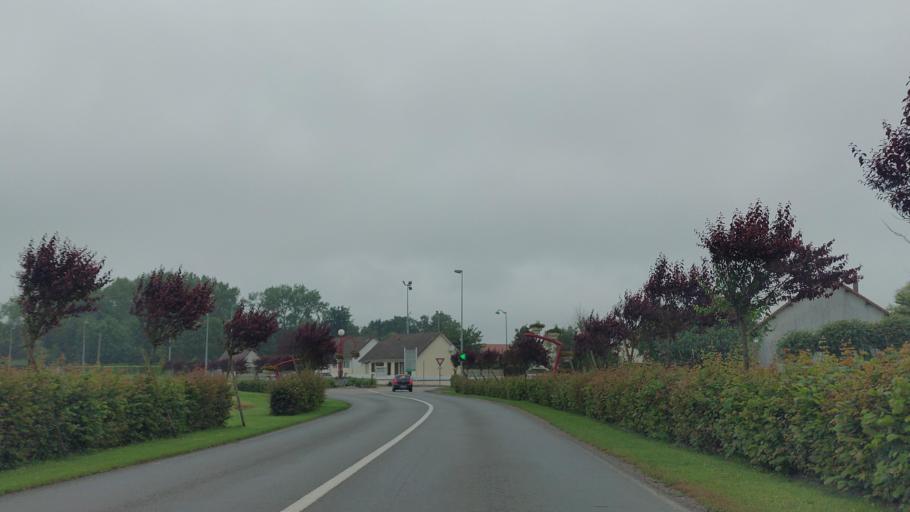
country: FR
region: Picardie
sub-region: Departement de la Somme
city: Bethencourt-sur-Mer
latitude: 50.0707
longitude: 1.5079
